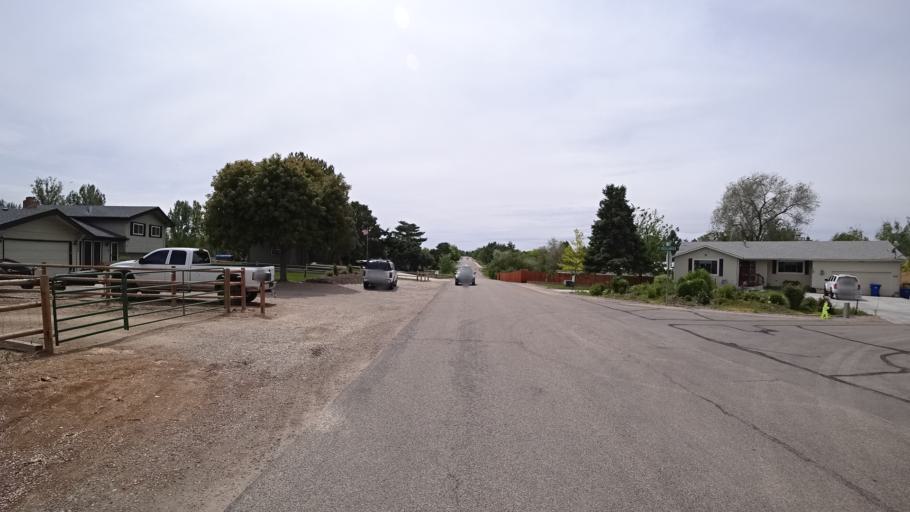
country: US
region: Idaho
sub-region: Ada County
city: Meridian
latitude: 43.5555
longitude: -116.3244
